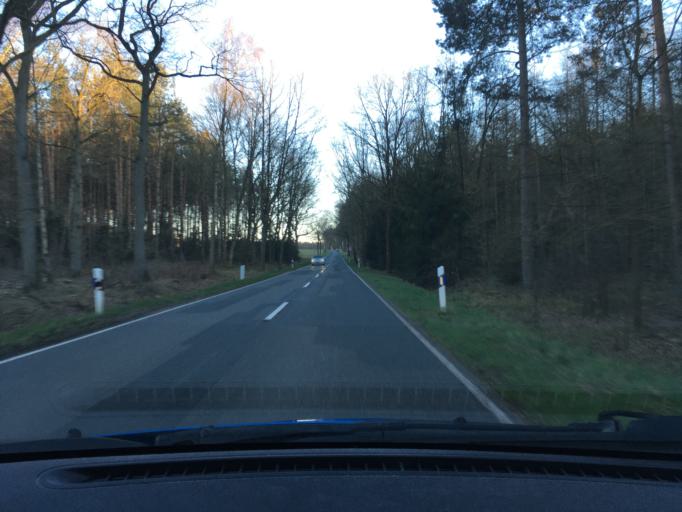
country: DE
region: Lower Saxony
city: Bleckede
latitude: 53.2523
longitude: 10.7454
